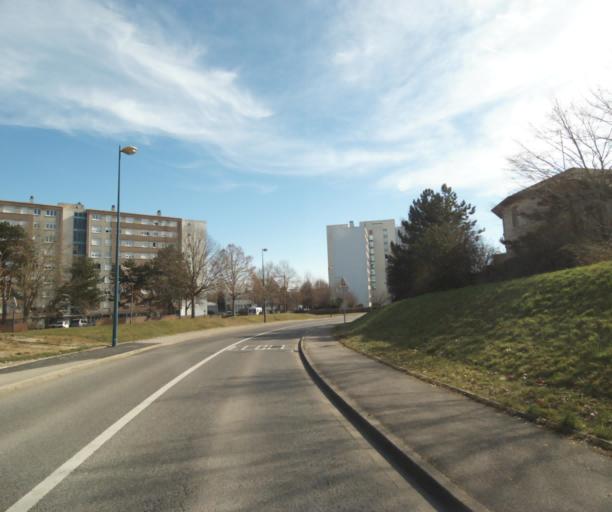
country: FR
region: Lorraine
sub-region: Departement de Meurthe-et-Moselle
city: Laxou
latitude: 48.6786
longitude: 6.1430
